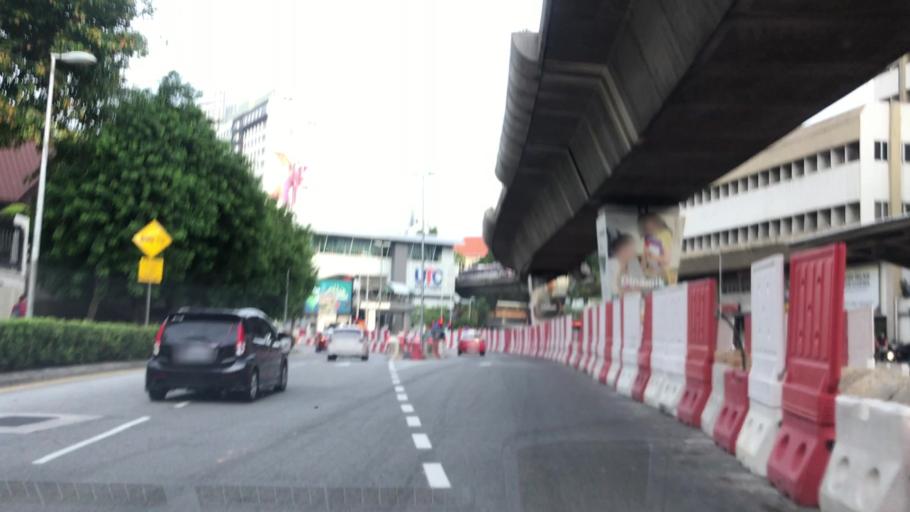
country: MY
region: Kuala Lumpur
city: Kuala Lumpur
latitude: 3.1469
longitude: 101.6988
